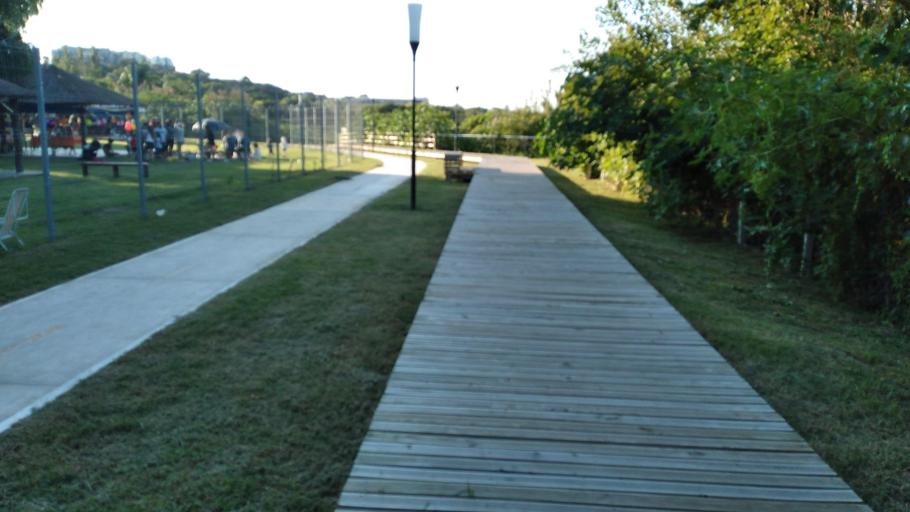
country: AR
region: Buenos Aires
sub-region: Partido de Vicente Lopez
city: Olivos
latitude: -34.4981
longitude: -58.4786
